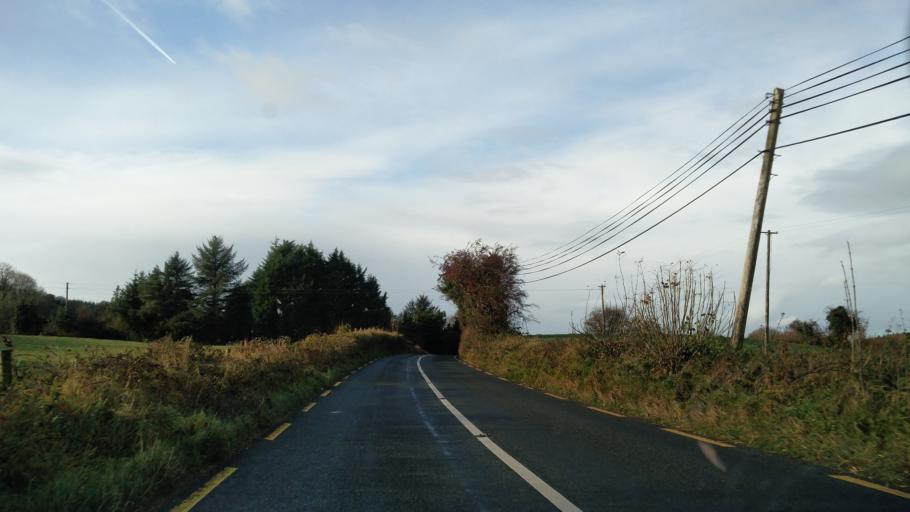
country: IE
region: Connaught
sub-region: Maigh Eo
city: Westport
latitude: 53.7861
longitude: -9.4880
